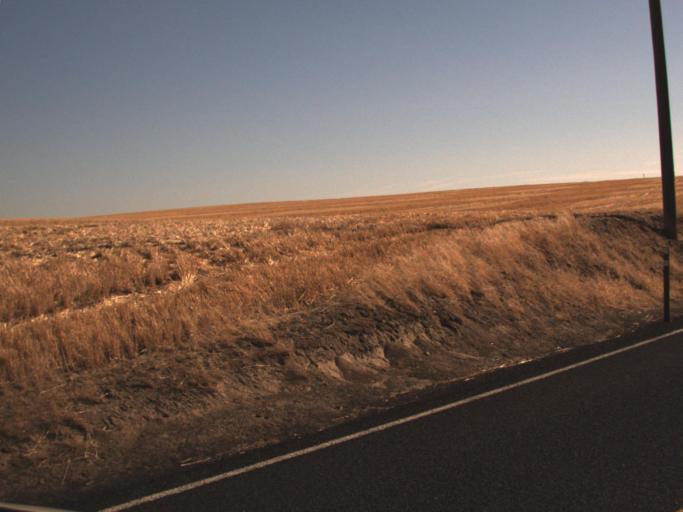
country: US
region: Washington
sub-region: Adams County
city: Ritzville
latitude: 46.9165
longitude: -118.5673
